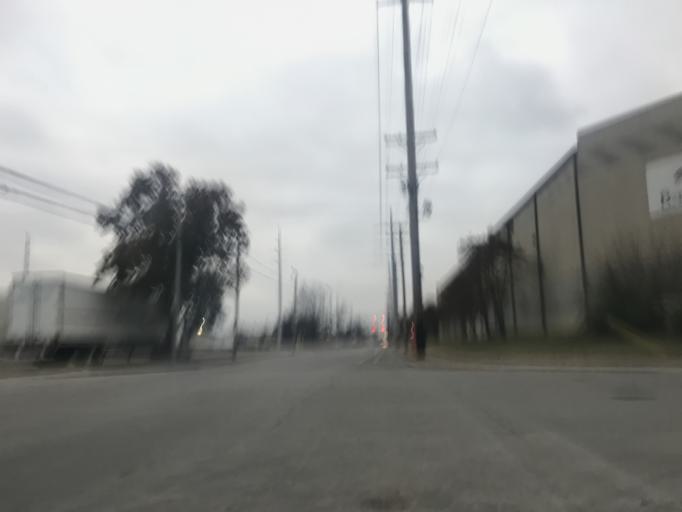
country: US
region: Kentucky
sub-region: Jefferson County
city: Louisville
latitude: 38.2422
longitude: -85.7726
